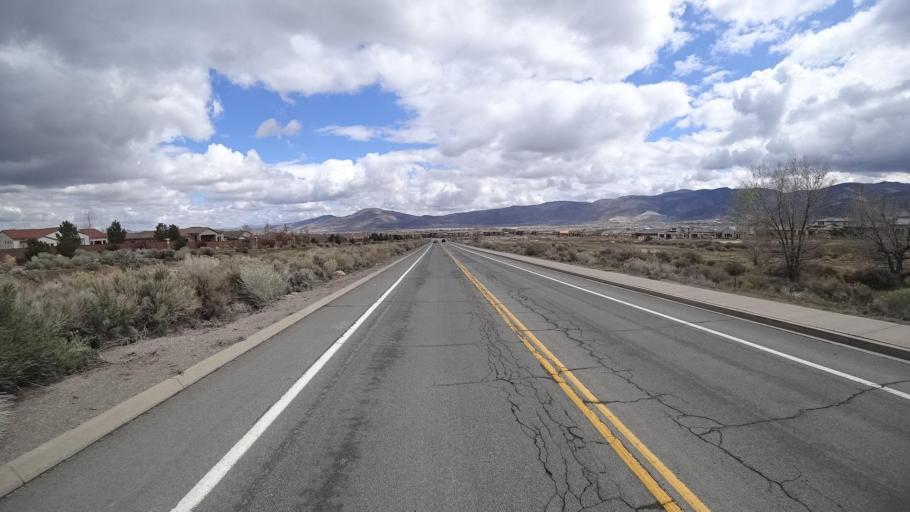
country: US
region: Nevada
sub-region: Washoe County
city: Sparks
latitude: 39.4052
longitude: -119.7660
